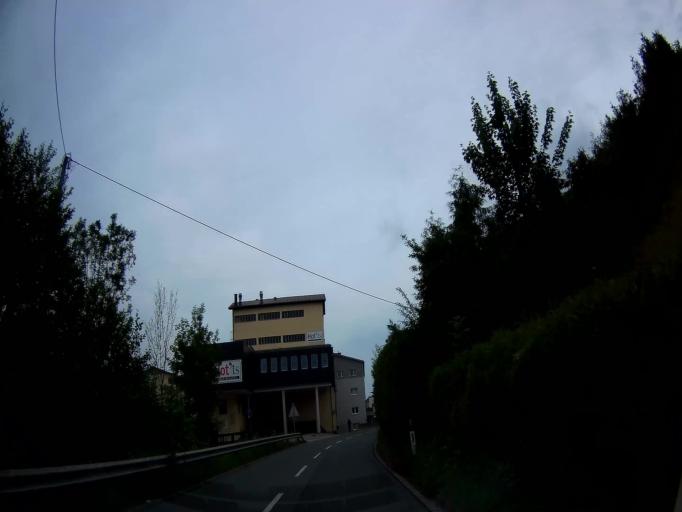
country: AT
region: Salzburg
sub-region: Politischer Bezirk Salzburg-Umgebung
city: Mattsee
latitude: 48.0980
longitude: 13.1493
